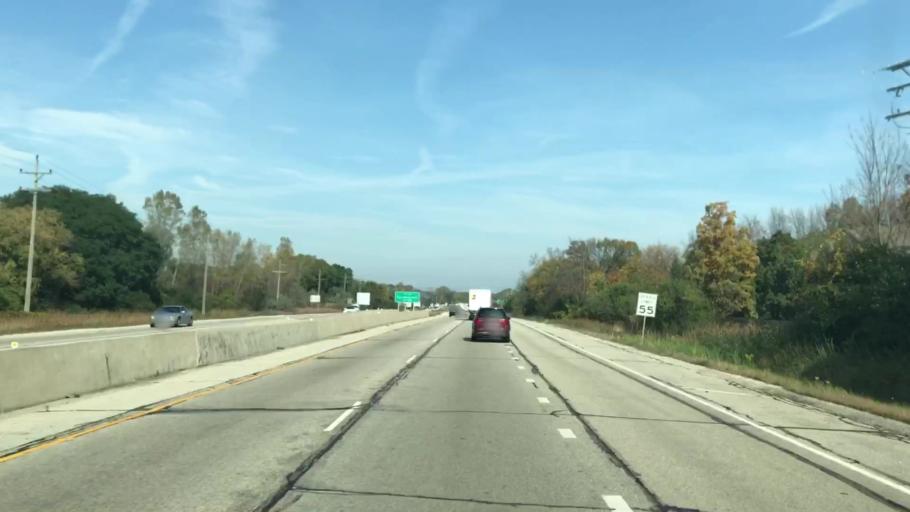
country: US
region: Wisconsin
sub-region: Milwaukee County
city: River Hills
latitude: 43.1811
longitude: -87.9193
